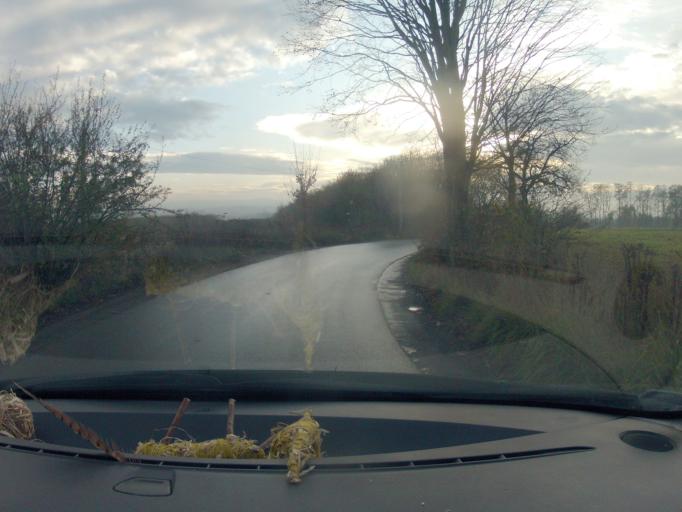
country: PL
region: Lesser Poland Voivodeship
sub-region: Krakow
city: Sidzina
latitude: 49.9999
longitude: 19.8867
